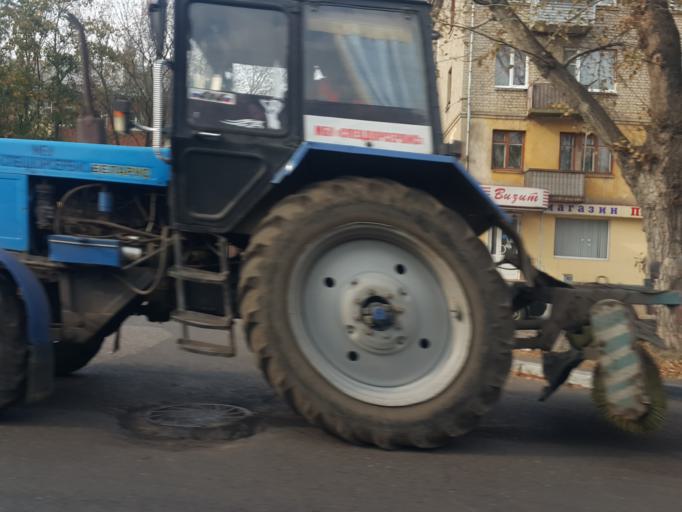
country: RU
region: Tambov
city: Bokino
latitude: 52.6818
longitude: 41.4630
